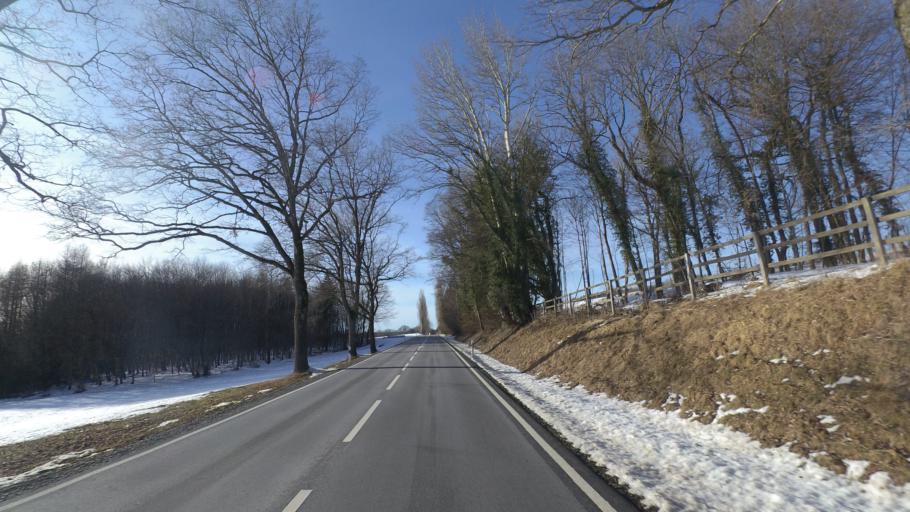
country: DE
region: Bavaria
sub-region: Upper Bavaria
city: Chieming
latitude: 47.9206
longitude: 12.5041
